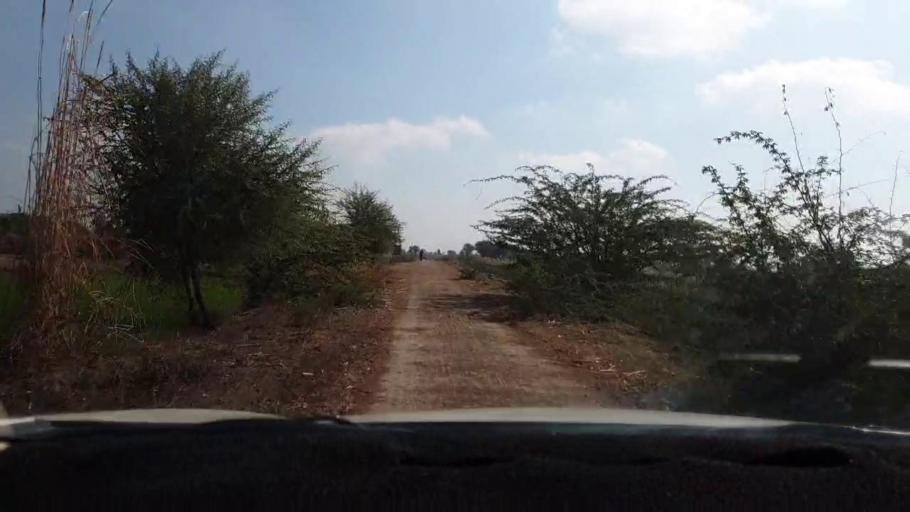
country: PK
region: Sindh
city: Berani
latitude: 25.7636
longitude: 68.8656
